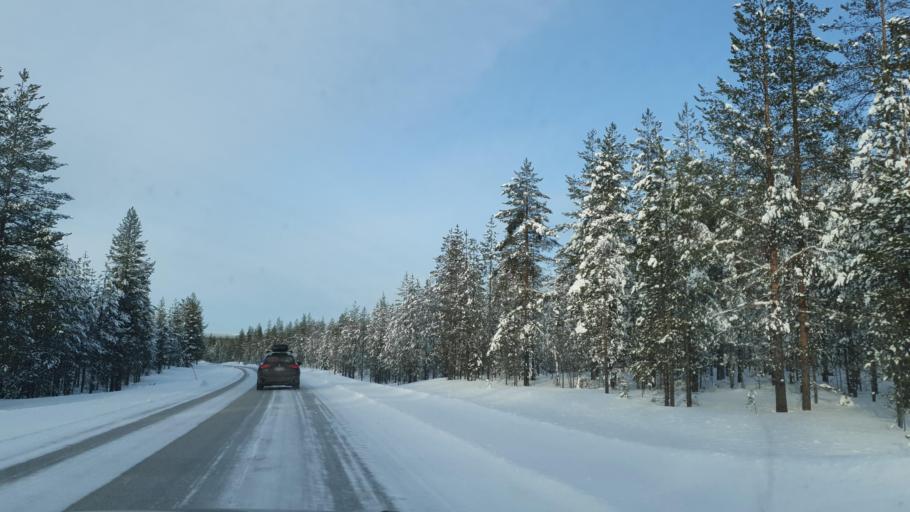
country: FI
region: Lapland
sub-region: Tunturi-Lappi
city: Kolari
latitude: 67.5039
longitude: 23.9054
